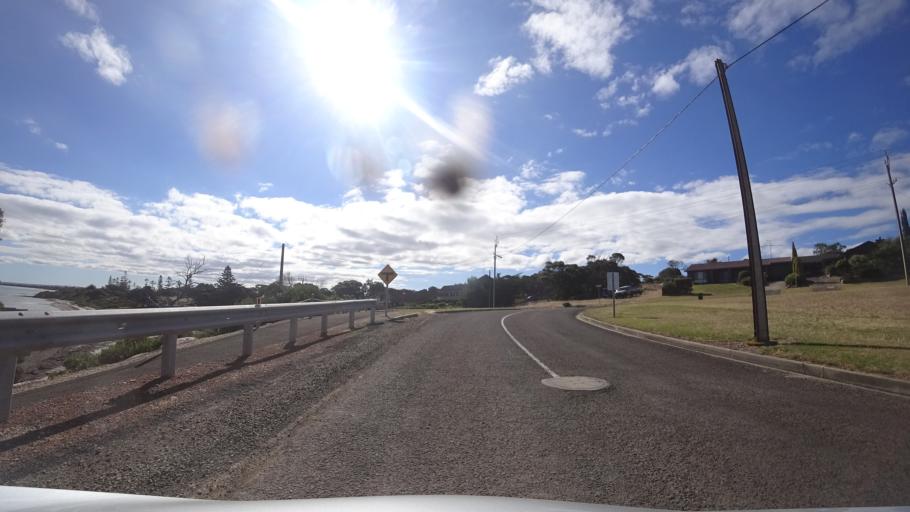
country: AU
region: South Australia
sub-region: Kangaroo Island
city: Kingscote
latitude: -35.6599
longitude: 137.6322
